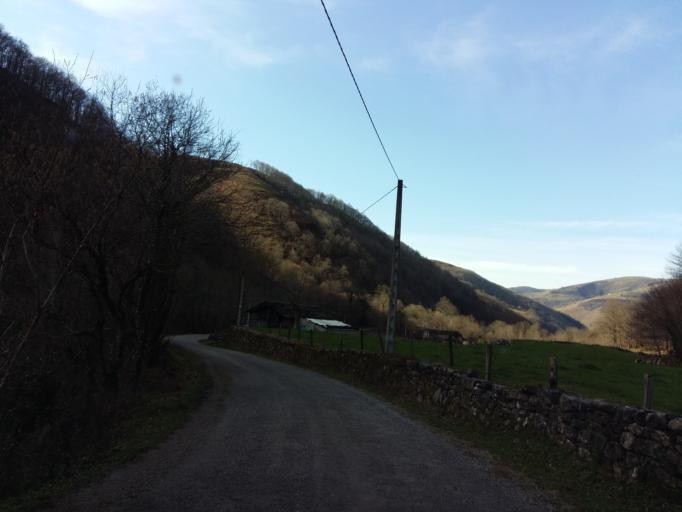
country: ES
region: Cantabria
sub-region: Provincia de Cantabria
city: Vega de Pas
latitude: 43.1366
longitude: -3.7900
